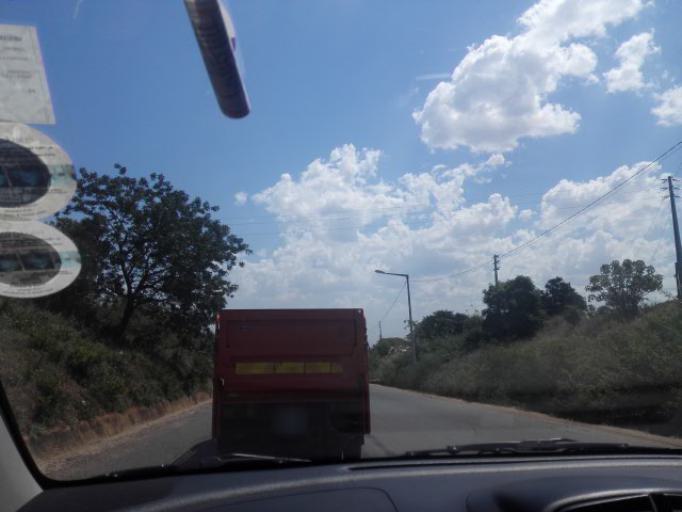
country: MZ
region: Maputo
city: Matola
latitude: -25.9625
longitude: 32.4483
